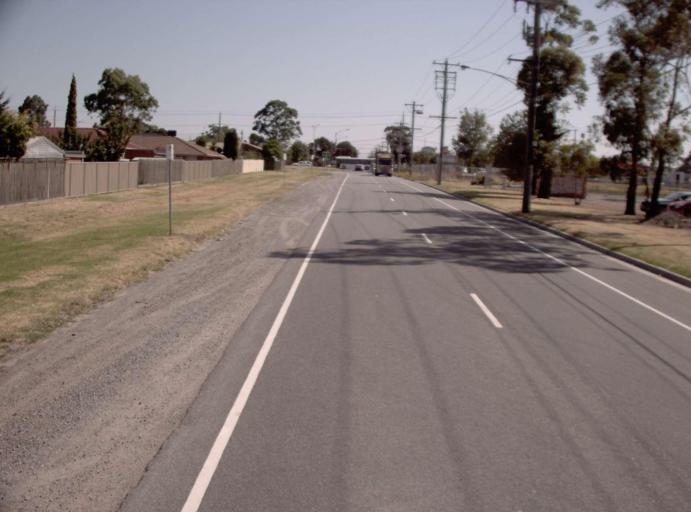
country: AU
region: Victoria
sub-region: Greater Dandenong
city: Keysborough
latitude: -37.9971
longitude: 145.1813
